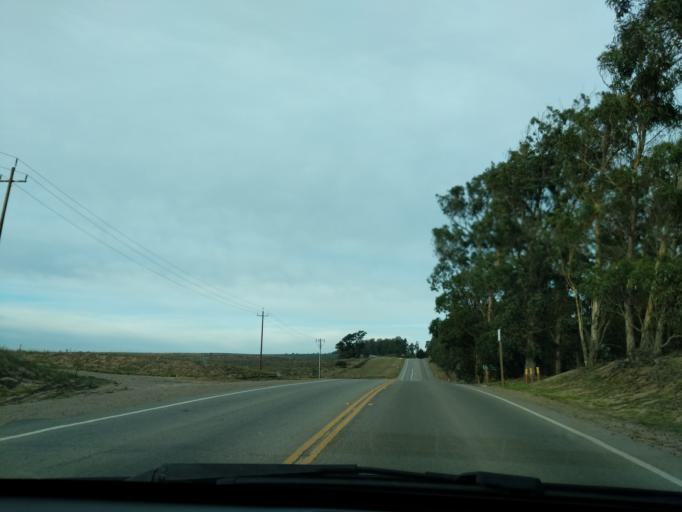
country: US
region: California
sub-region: San Luis Obispo County
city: Callender
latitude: 35.0212
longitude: -120.5633
